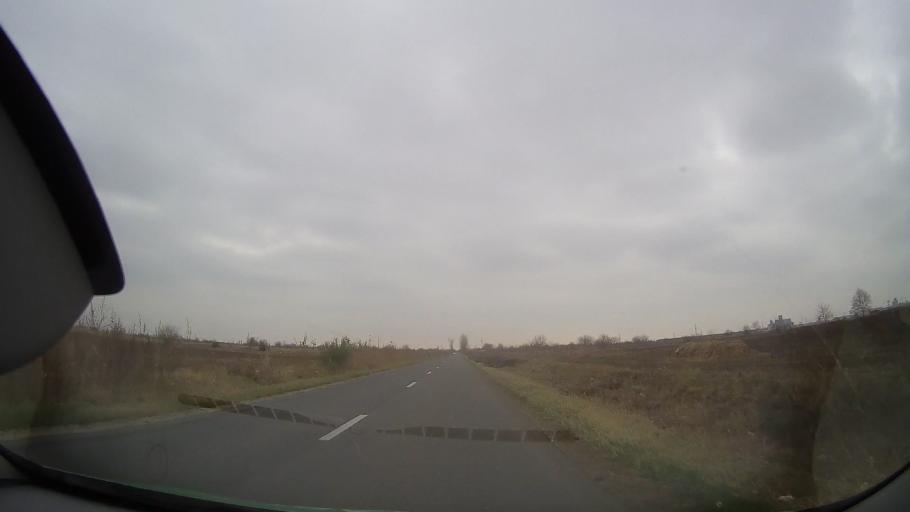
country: RO
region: Ialomita
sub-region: Comuna Manasia
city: Manasia
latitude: 44.7195
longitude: 26.6852
